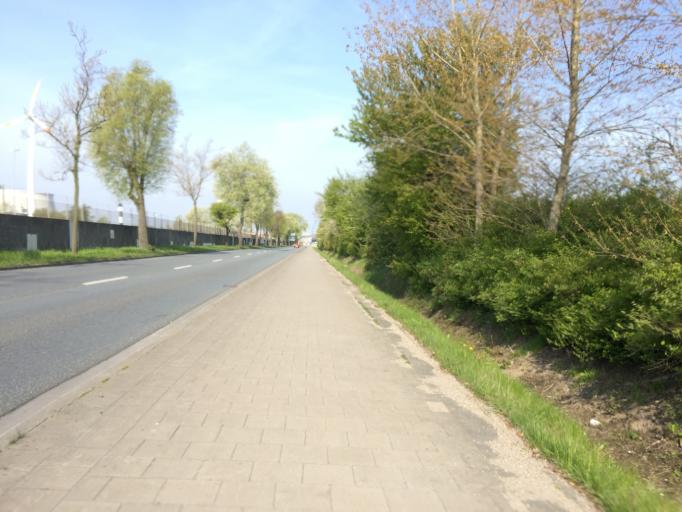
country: DE
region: Hamburg
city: Harburg
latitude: 53.4930
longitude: 9.9647
